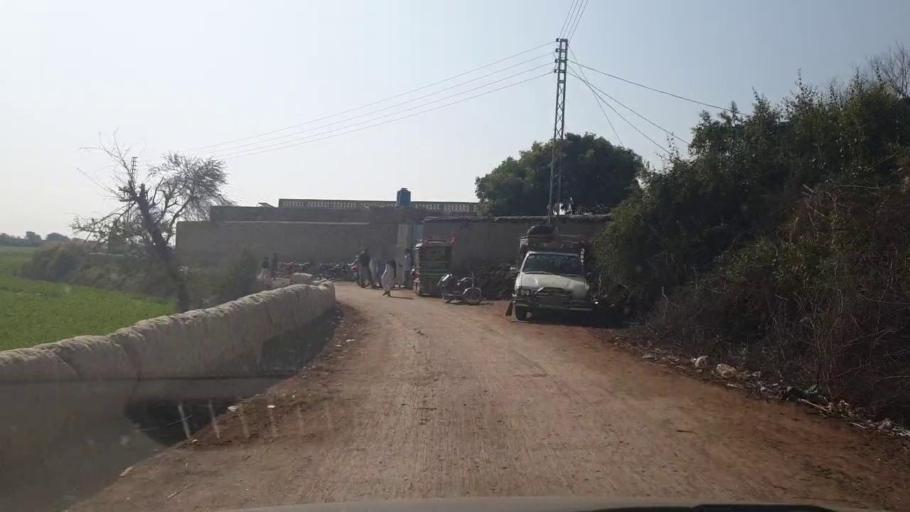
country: PK
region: Sindh
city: Tando Adam
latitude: 25.7512
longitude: 68.6149
